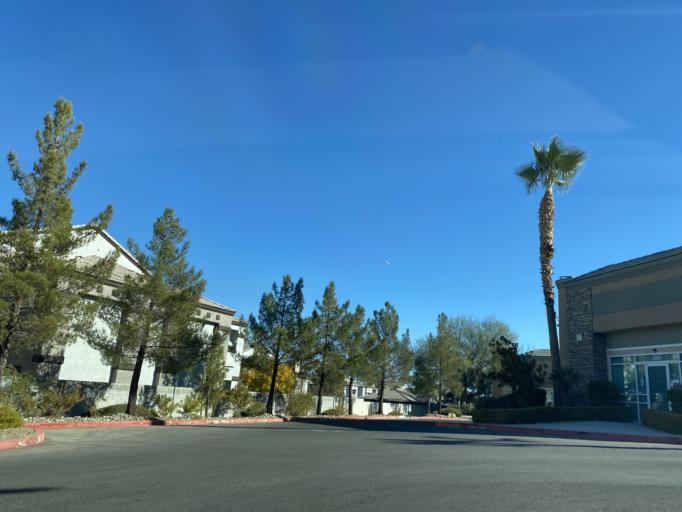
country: US
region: Nevada
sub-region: Clark County
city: Spring Valley
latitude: 36.0684
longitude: -115.2515
